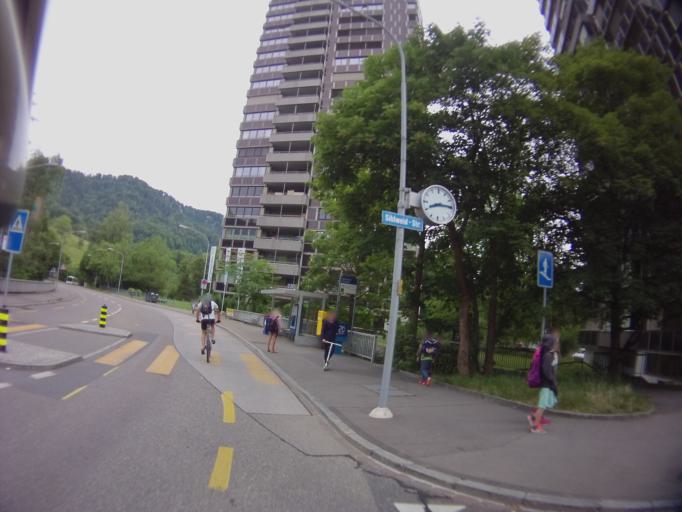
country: CH
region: Zurich
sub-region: Bezirk Zuerich
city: Zuerich (Kreis 2) / Mittel-Leimbach
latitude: 47.3261
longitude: 8.5152
